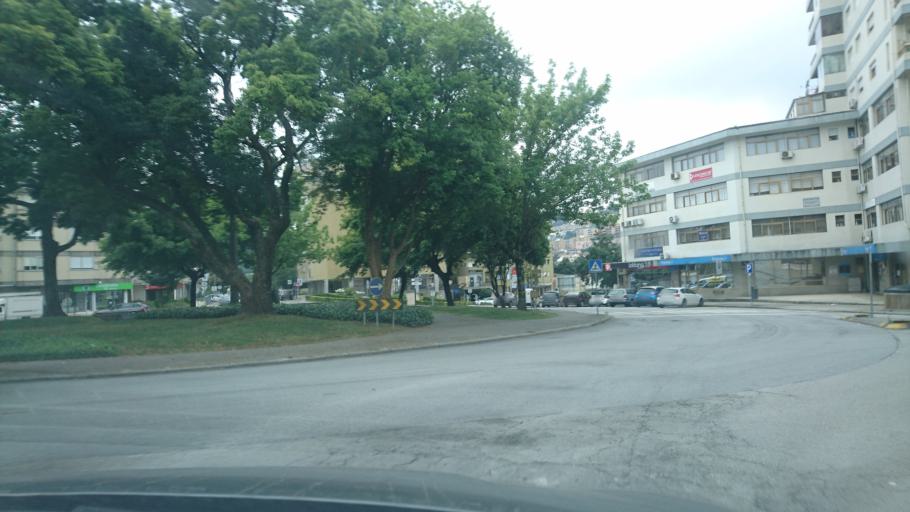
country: PT
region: Porto
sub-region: Valongo
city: Valongo
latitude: 41.1940
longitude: -8.5013
